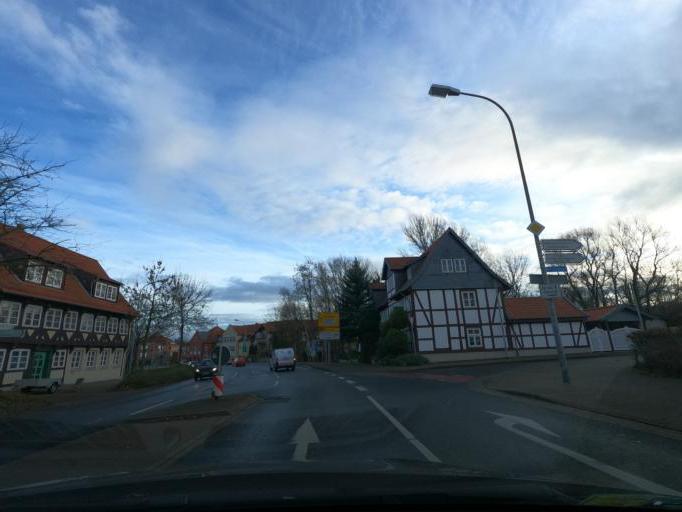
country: DE
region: Lower Saxony
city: Wolfenbuettel
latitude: 52.1630
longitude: 10.5256
